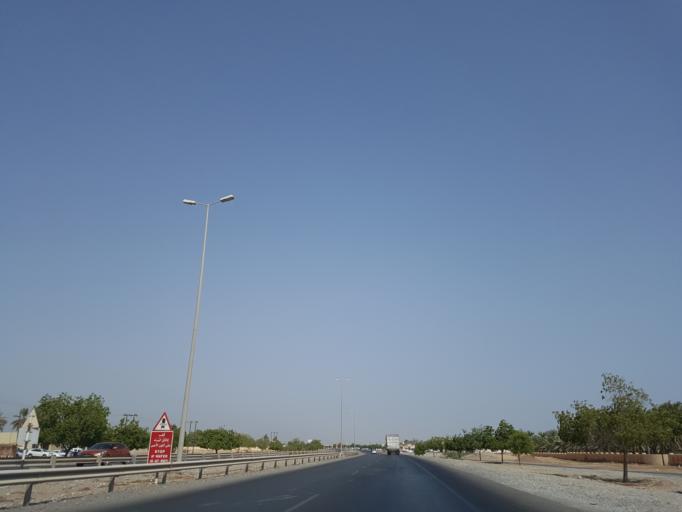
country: OM
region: Al Batinah
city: As Suwayq
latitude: 23.7501
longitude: 57.6142
